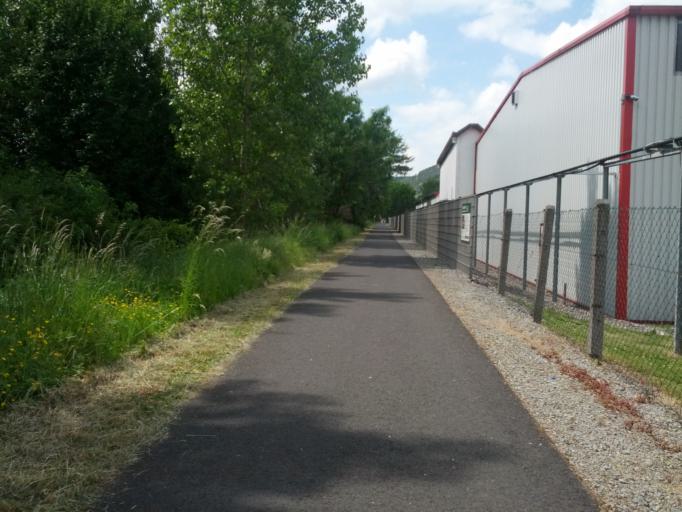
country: DE
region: Thuringia
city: Treffurt
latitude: 51.1326
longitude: 10.2444
